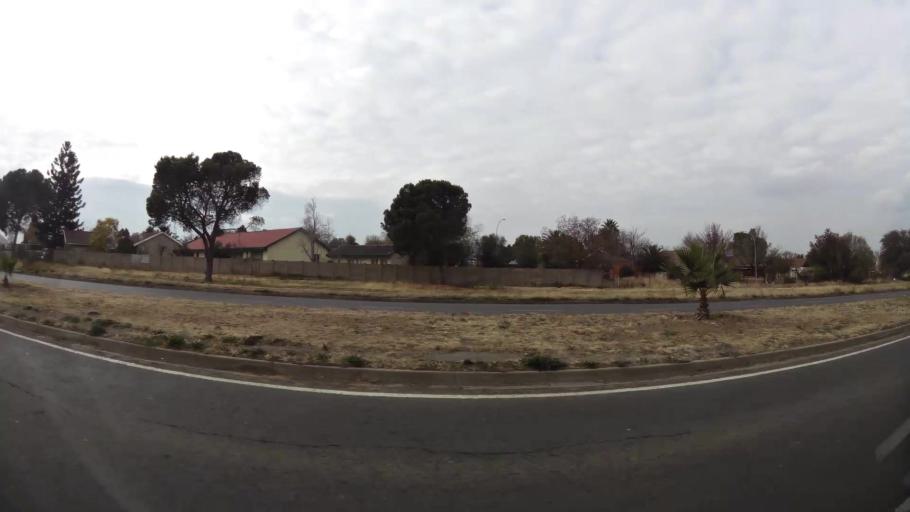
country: ZA
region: Orange Free State
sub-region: Mangaung Metropolitan Municipality
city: Bloemfontein
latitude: -29.1582
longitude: 26.1859
